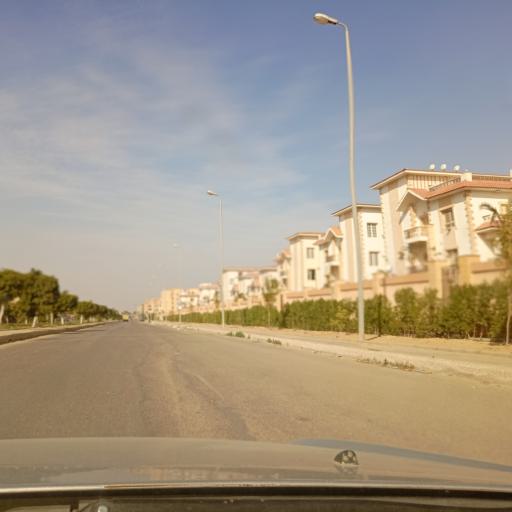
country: EG
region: Muhafazat al Qalyubiyah
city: Al Khankah
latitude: 30.0389
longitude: 31.4852
